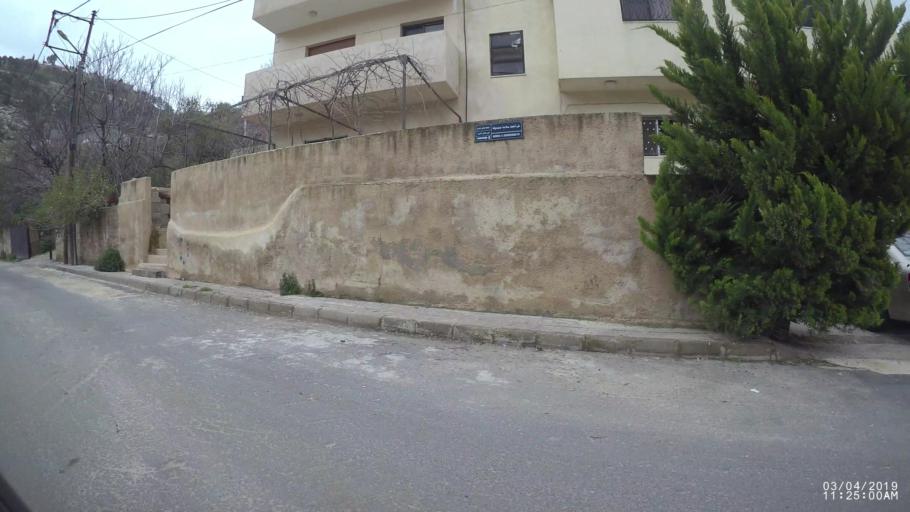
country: JO
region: Amman
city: Wadi as Sir
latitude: 31.9563
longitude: 35.8176
